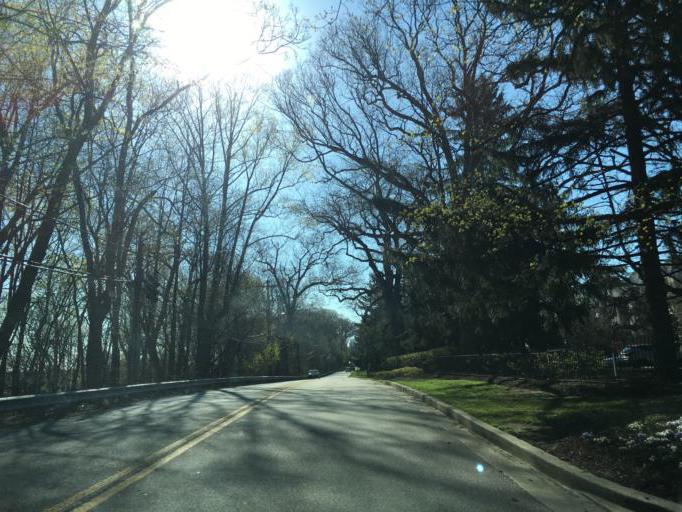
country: US
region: Maryland
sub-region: Baltimore County
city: Lutherville
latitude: 39.4101
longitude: -76.6235
